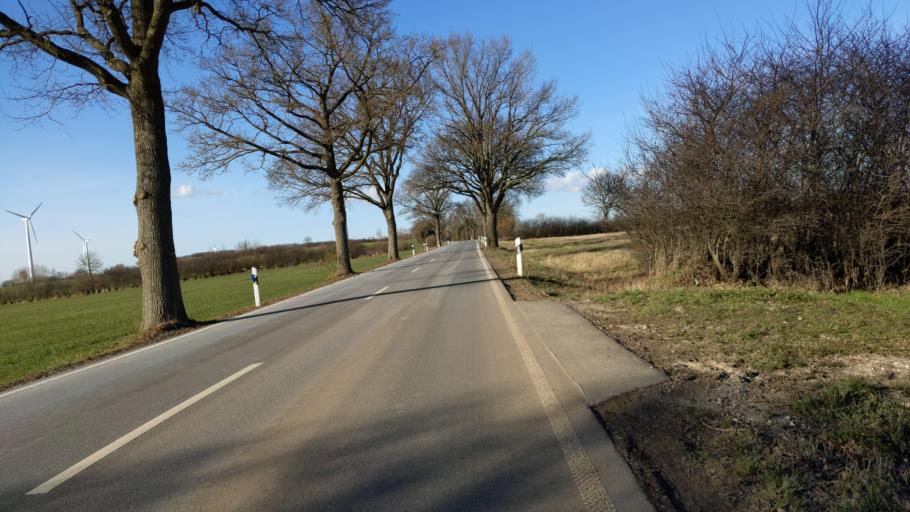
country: DE
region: Schleswig-Holstein
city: Susel
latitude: 54.0520
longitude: 10.6539
